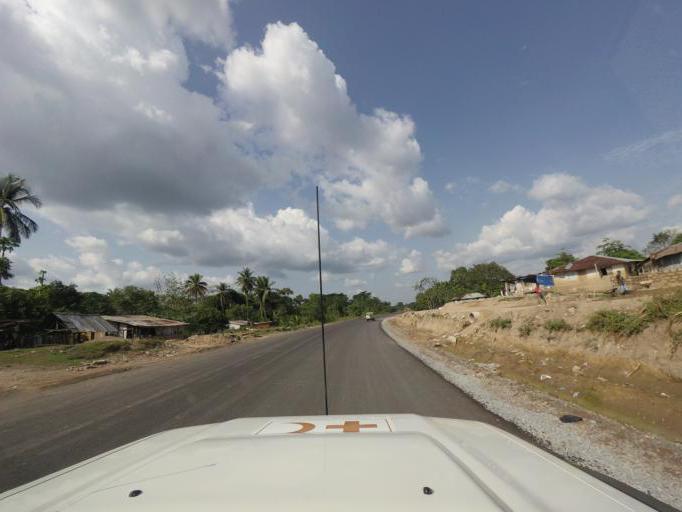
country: LR
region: Bong
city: Gbarnga
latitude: 7.0111
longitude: -9.5644
